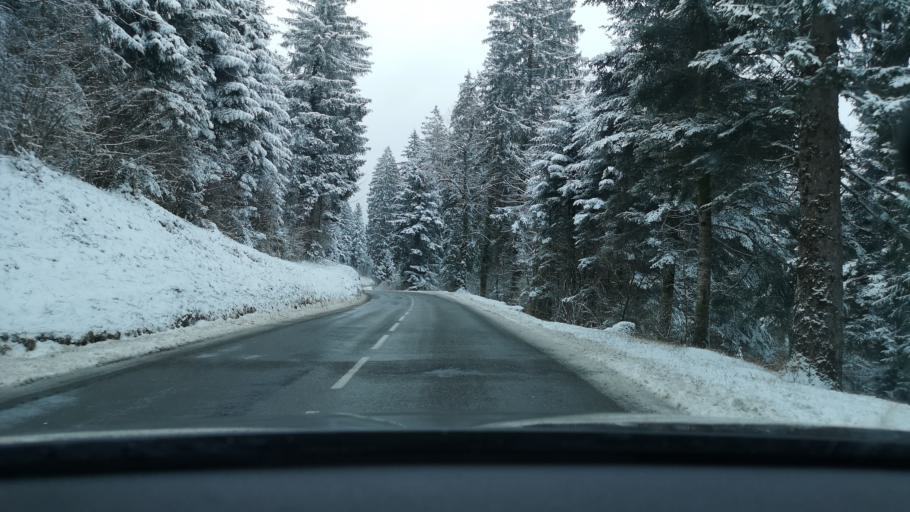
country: FR
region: Rhone-Alpes
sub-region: Departement de l'Ain
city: Oyonnax
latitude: 46.2536
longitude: 5.6748
